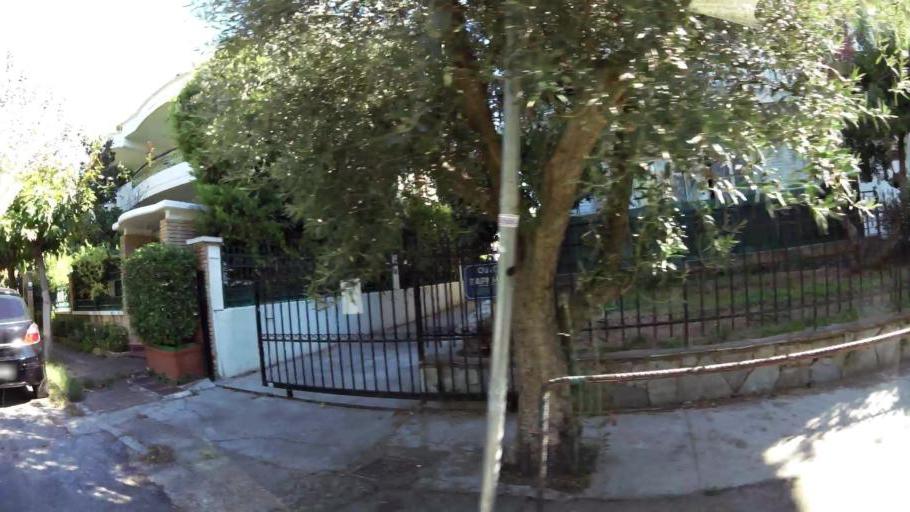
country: GR
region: Attica
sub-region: Nomarchia Athinas
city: Vrilissia
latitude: 38.0313
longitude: 23.8171
